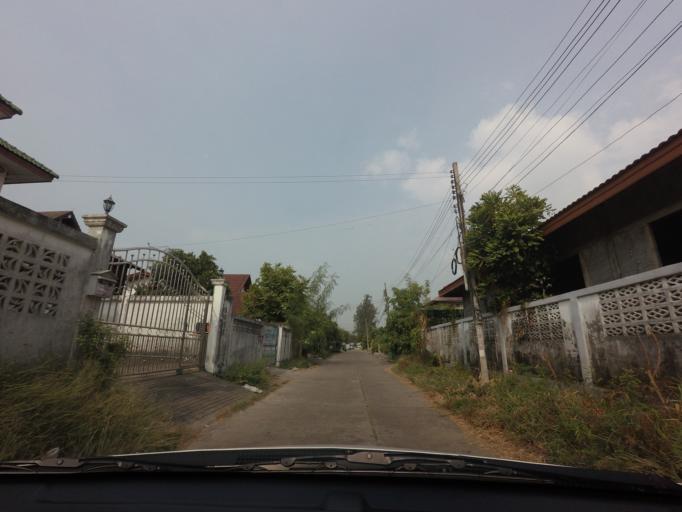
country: TH
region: Bangkok
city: Nong Khaem
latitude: 13.7419
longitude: 100.3418
